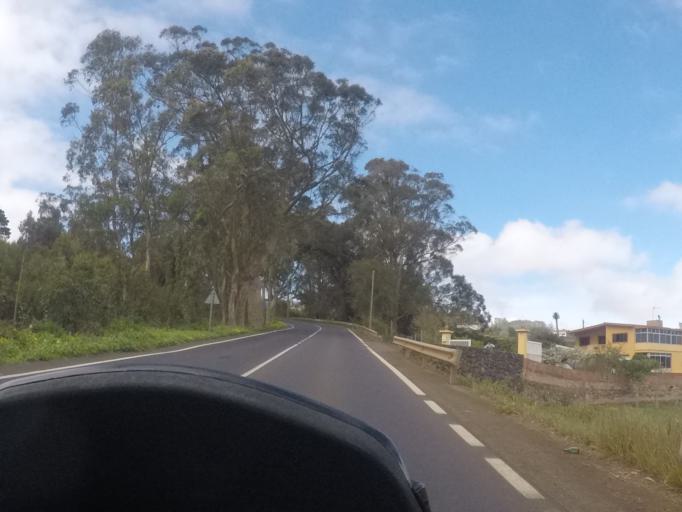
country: ES
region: Canary Islands
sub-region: Provincia de Santa Cruz de Tenerife
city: La Laguna
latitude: 28.4609
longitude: -16.3577
